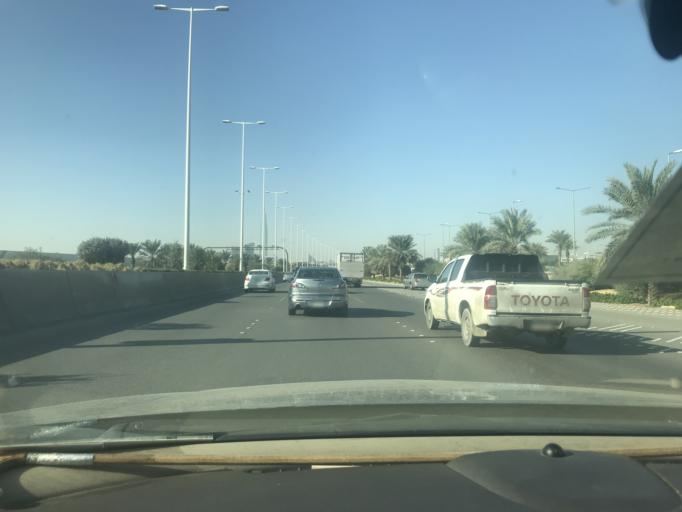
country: SA
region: Ar Riyad
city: Riyadh
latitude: 24.7242
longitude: 46.7012
